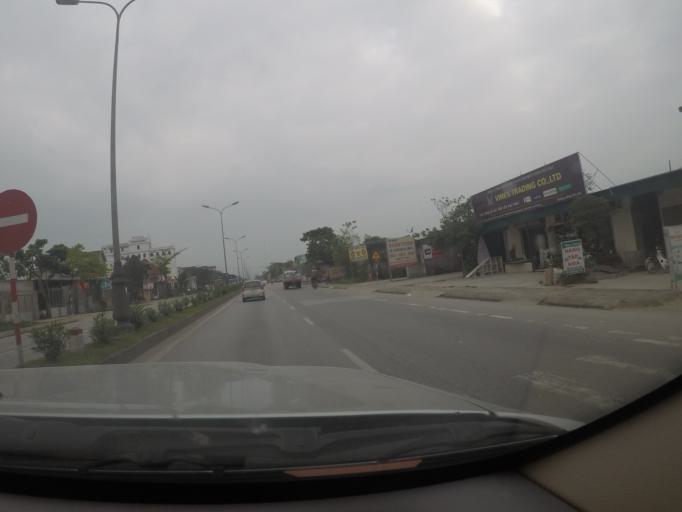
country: VN
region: Nghe An
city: Dien Chau
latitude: 18.9610
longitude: 105.6016
